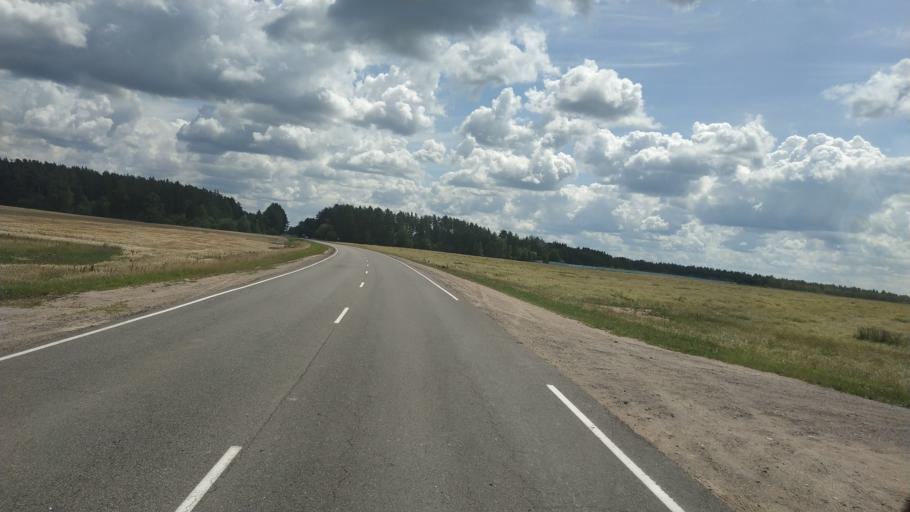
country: BY
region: Mogilev
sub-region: Mahilyowski Rayon
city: Veyno
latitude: 53.8324
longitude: 30.4038
